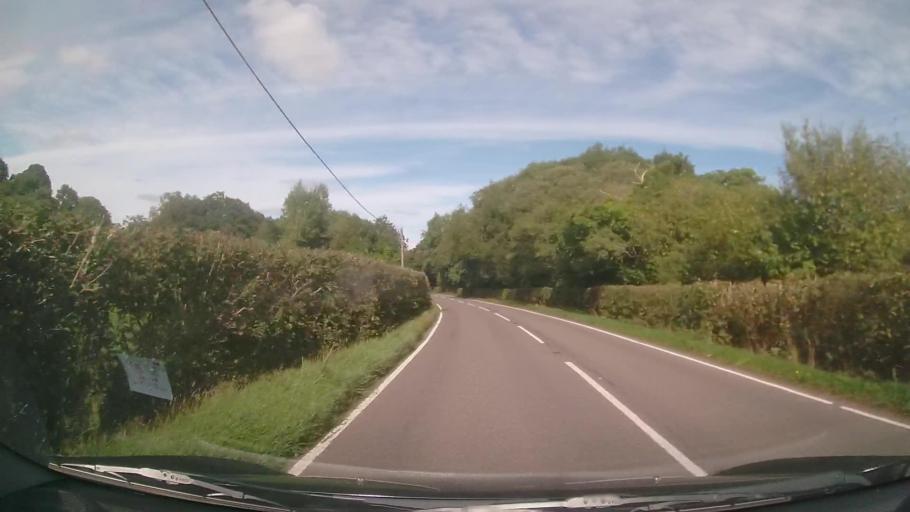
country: GB
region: England
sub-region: Shropshire
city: Lydham
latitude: 52.5496
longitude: -2.9957
